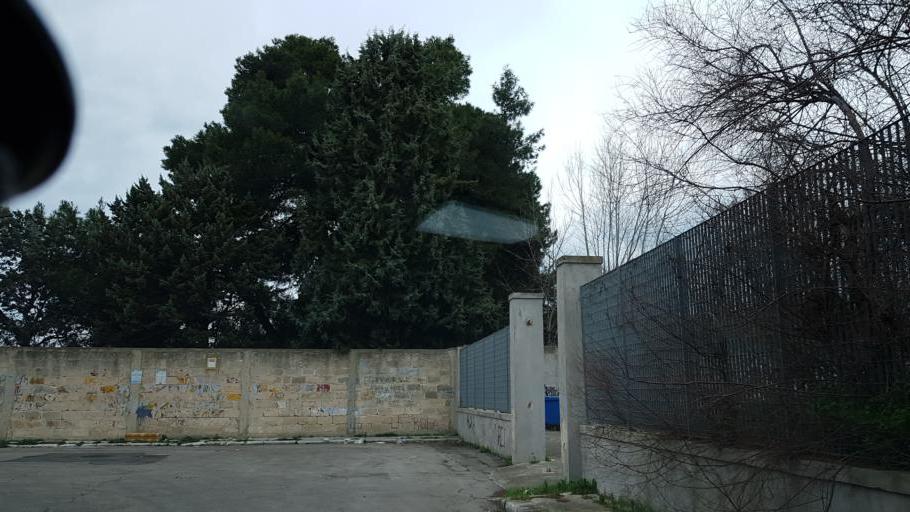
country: IT
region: Apulia
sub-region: Provincia di Brindisi
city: La Rosa
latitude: 40.6098
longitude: 17.9527
